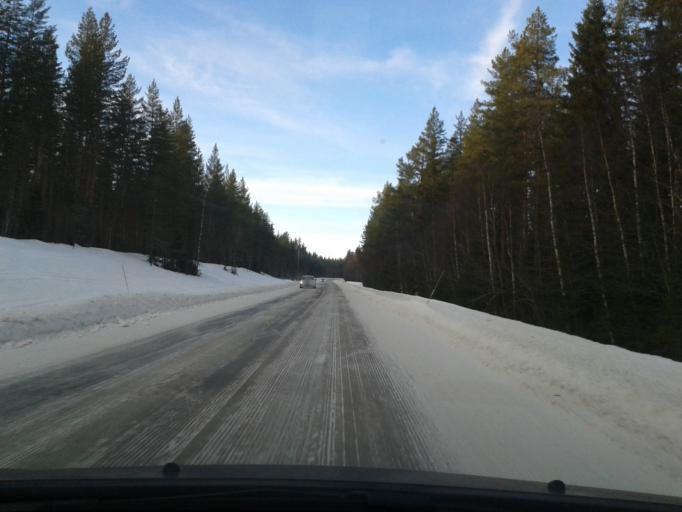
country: SE
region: Vaesternorrland
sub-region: OErnskoeldsviks Kommun
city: Bredbyn
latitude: 63.6012
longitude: 17.9081
